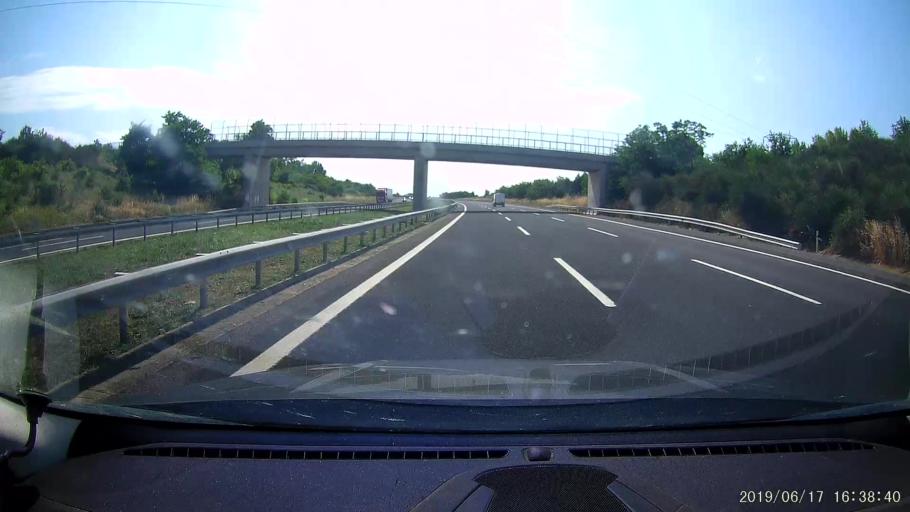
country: TR
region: Kirklareli
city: Luleburgaz
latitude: 41.4472
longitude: 27.4357
